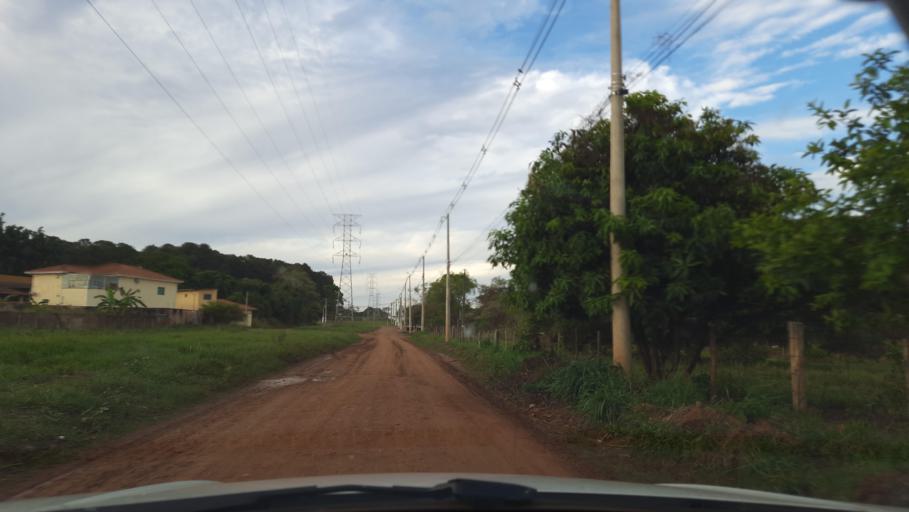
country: BR
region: Sao Paulo
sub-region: Casa Branca
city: Casa Branca
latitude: -21.7738
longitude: -47.0685
